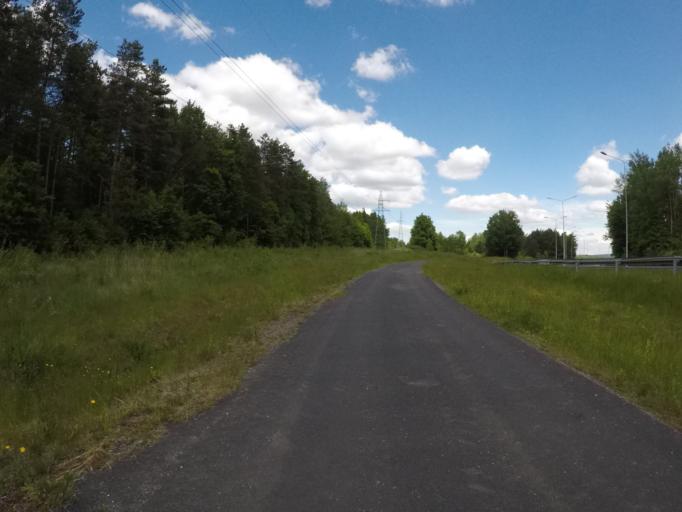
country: PL
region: Swietokrzyskie
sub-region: Powiat kielecki
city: Zagnansk
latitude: 50.9398
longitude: 20.6698
